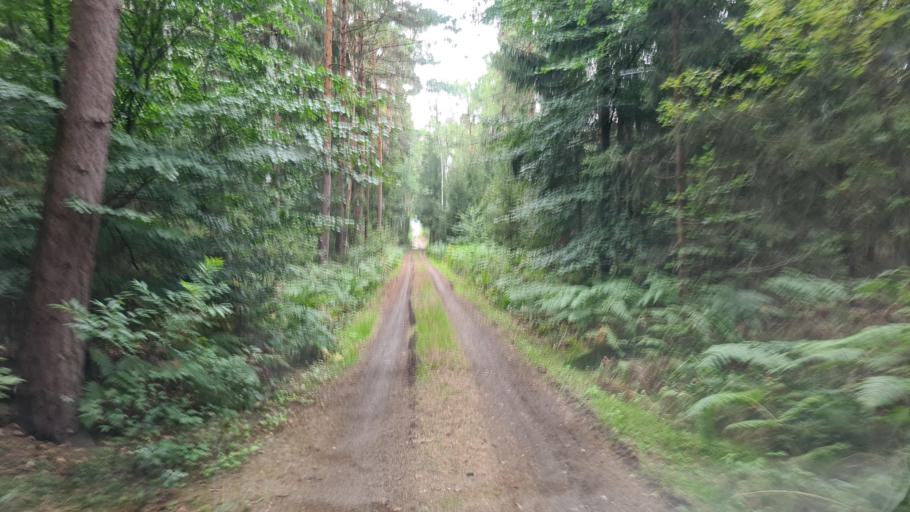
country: DE
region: Brandenburg
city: Schonborn
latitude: 51.6262
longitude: 13.5128
